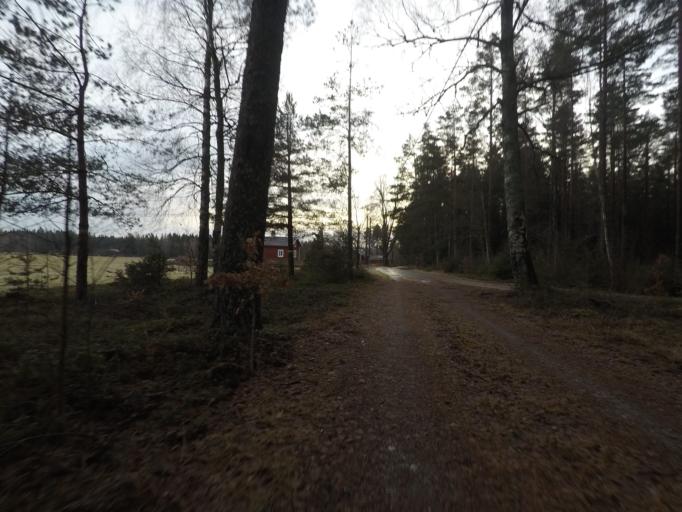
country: SE
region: Vaestmanland
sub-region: Kungsors Kommun
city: Kungsoer
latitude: 59.3424
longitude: 16.1189
